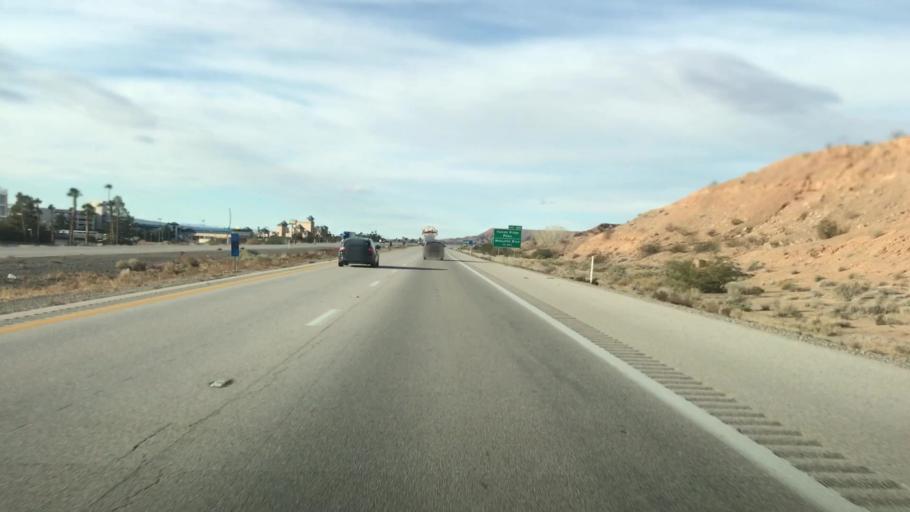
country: US
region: Nevada
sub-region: Clark County
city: Mesquite
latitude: 36.8082
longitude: -114.0930
